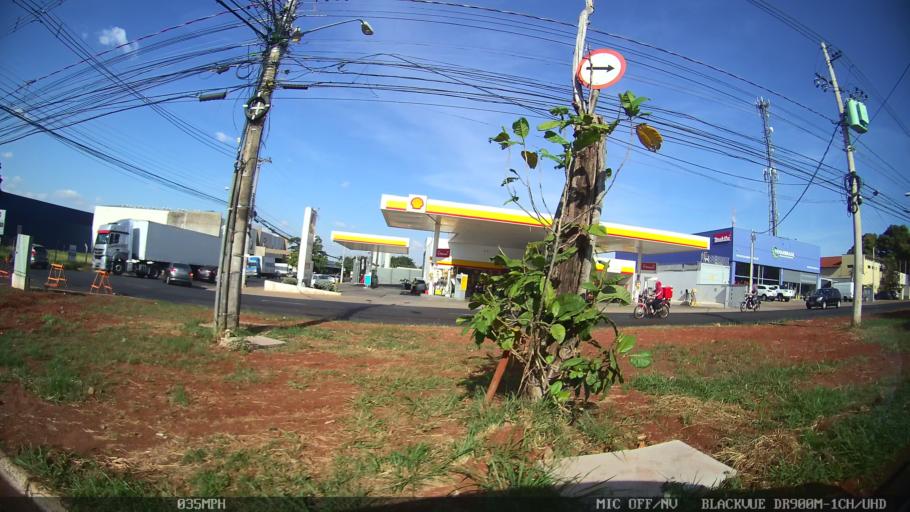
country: BR
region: Sao Paulo
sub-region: Ribeirao Preto
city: Ribeirao Preto
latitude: -21.1980
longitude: -47.7648
